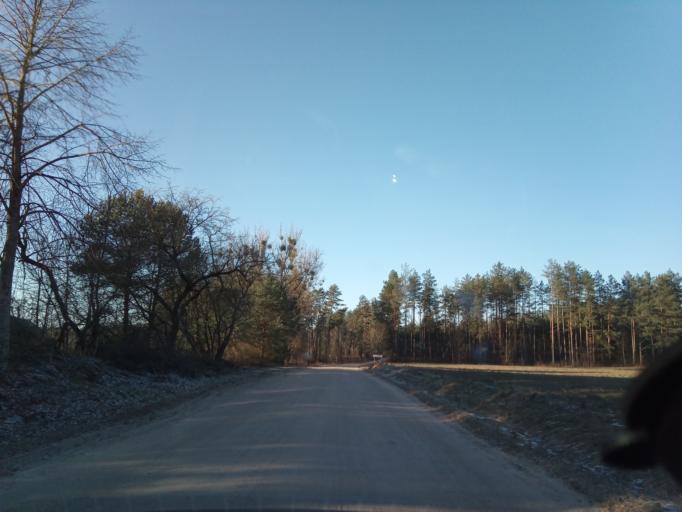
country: LT
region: Alytaus apskritis
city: Druskininkai
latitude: 53.9560
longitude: 23.8896
